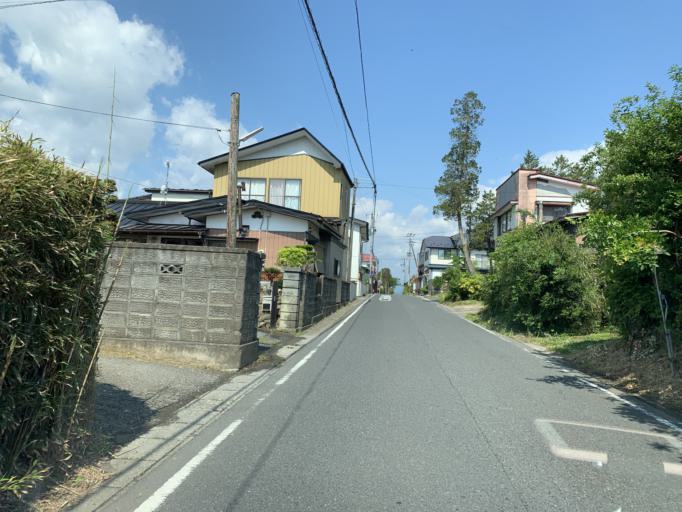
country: JP
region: Iwate
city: Ichinoseki
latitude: 38.7959
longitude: 141.0240
